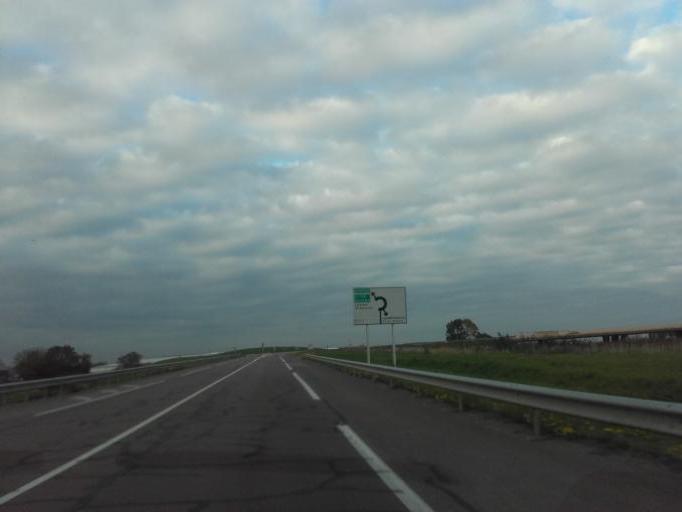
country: FR
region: Bourgogne
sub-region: Departement de Saone-et-Loire
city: Champforgeuil
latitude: 46.8240
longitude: 4.8295
